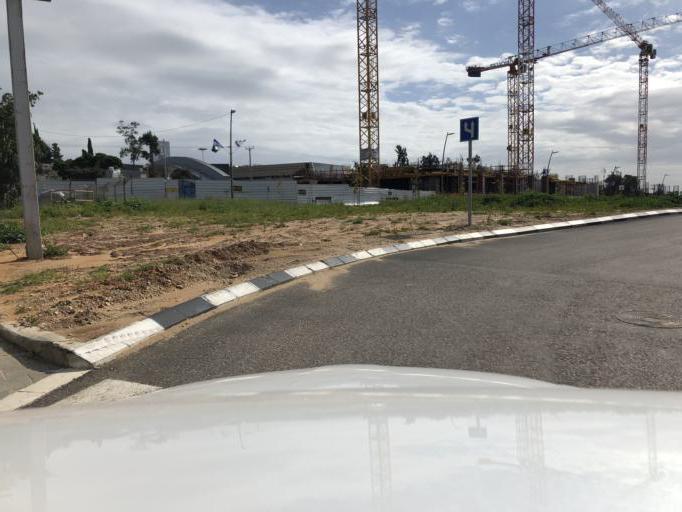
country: IL
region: Tel Aviv
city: Or Yehuda
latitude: 32.0510
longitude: 34.8406
